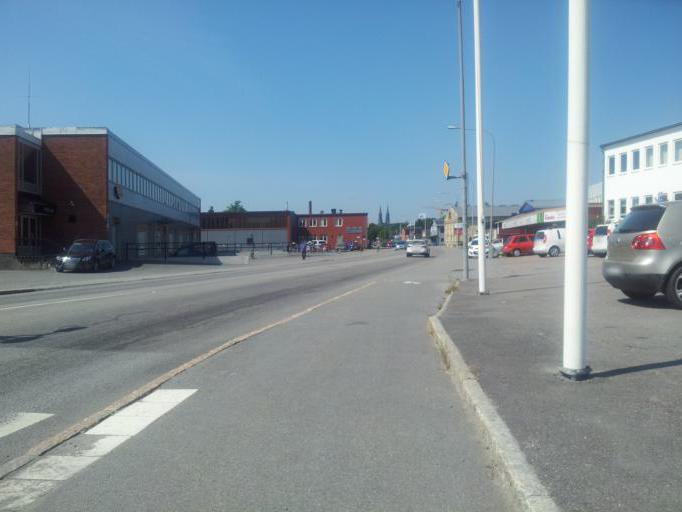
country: SE
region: Uppsala
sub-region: Uppsala Kommun
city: Uppsala
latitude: 59.8563
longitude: 17.6649
